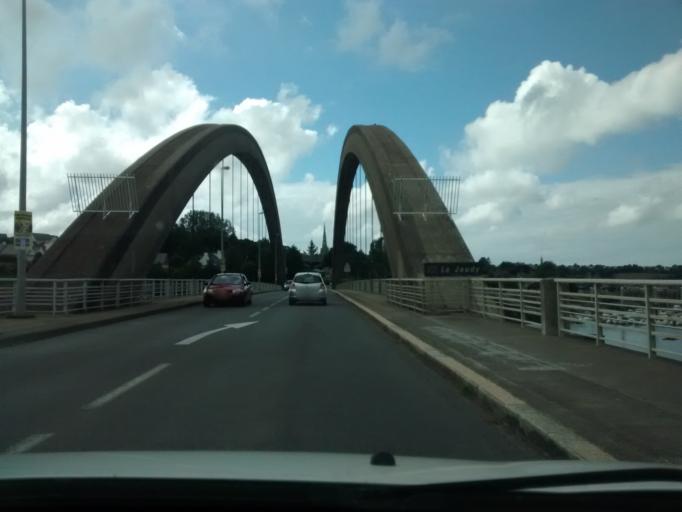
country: FR
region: Brittany
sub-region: Departement des Cotes-d'Armor
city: Minihy-Treguier
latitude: 48.7839
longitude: -3.2197
